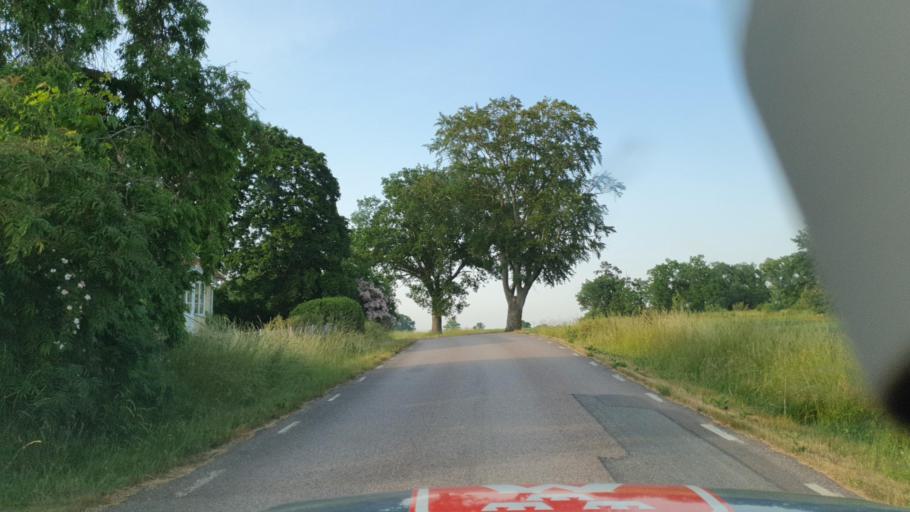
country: SE
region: Kalmar
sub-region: Kalmar Kommun
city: Ljungbyholm
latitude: 56.5169
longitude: 16.1396
